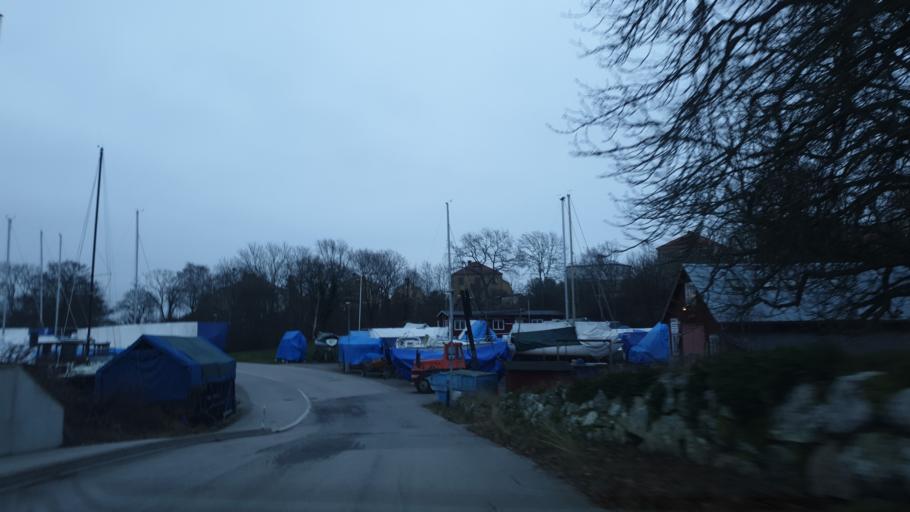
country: SE
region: Blekinge
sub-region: Karlskrona Kommun
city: Karlskrona
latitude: 56.1693
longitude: 15.5654
